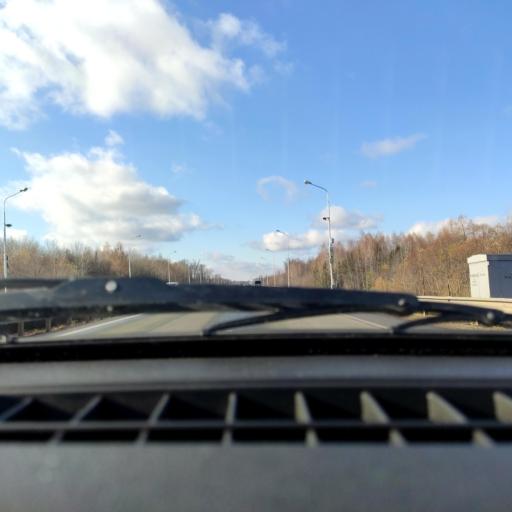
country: RU
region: Bashkortostan
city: Ufa
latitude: 54.6687
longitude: 56.0525
